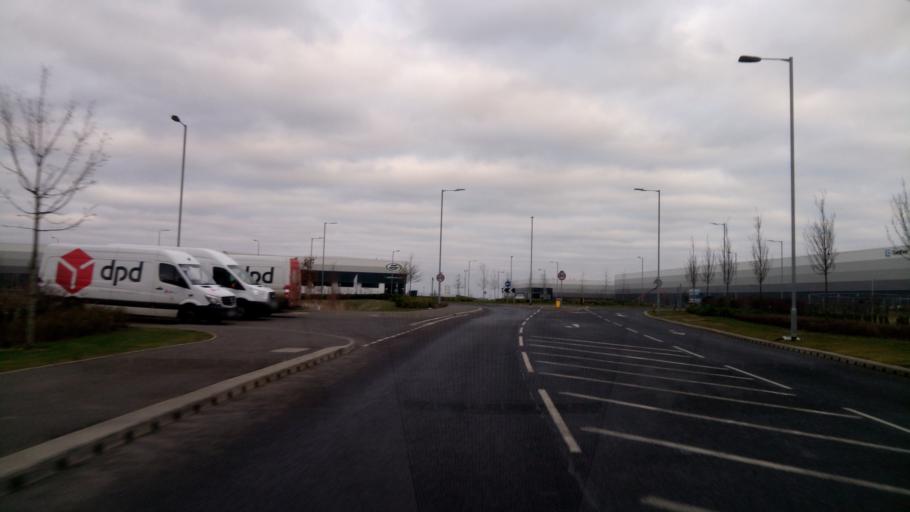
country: GB
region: England
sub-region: Cambridgeshire
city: Stilton
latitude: 52.5335
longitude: -0.3046
